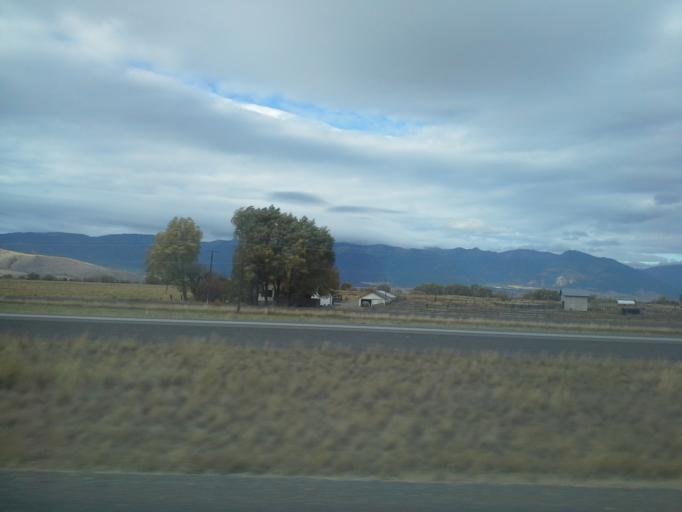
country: US
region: Oregon
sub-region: Baker County
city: Baker City
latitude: 44.8169
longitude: -117.8147
